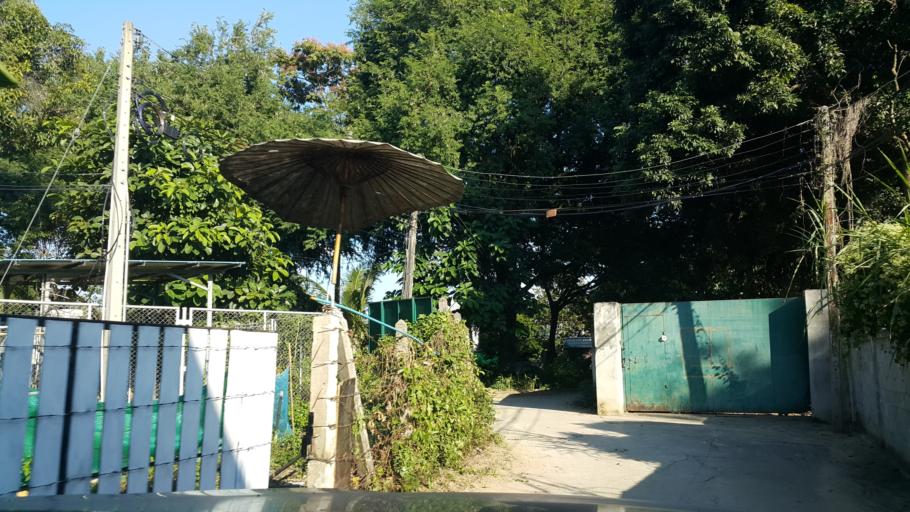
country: TH
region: Chiang Mai
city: Chiang Mai
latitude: 18.7682
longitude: 98.9552
